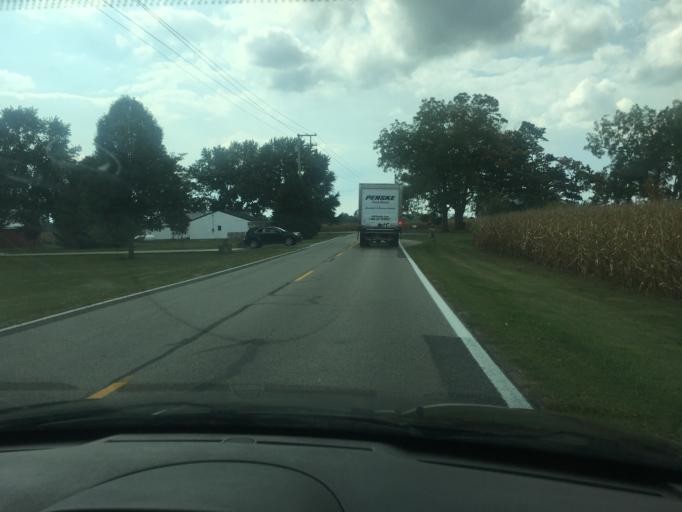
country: US
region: Ohio
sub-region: Champaign County
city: Urbana
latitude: 40.1592
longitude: -83.8122
